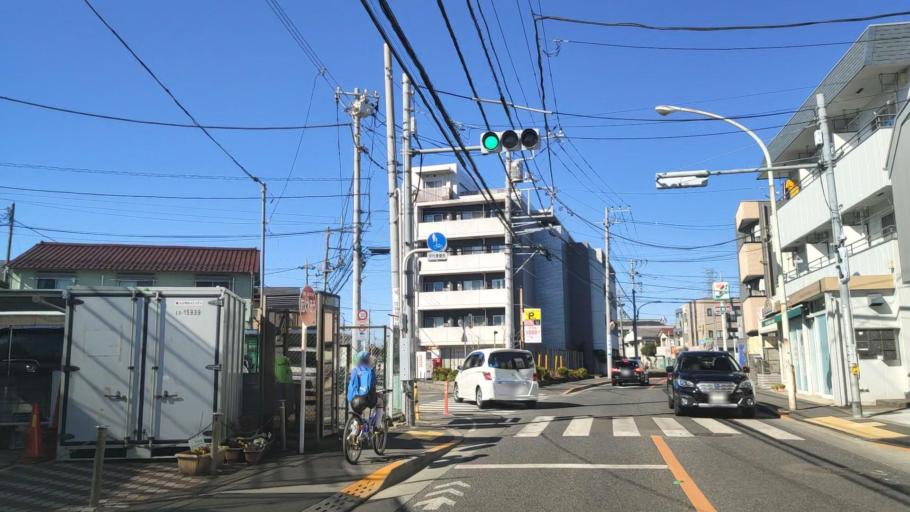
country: JP
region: Tokyo
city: Mitaka-shi
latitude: 35.6673
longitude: 139.5762
